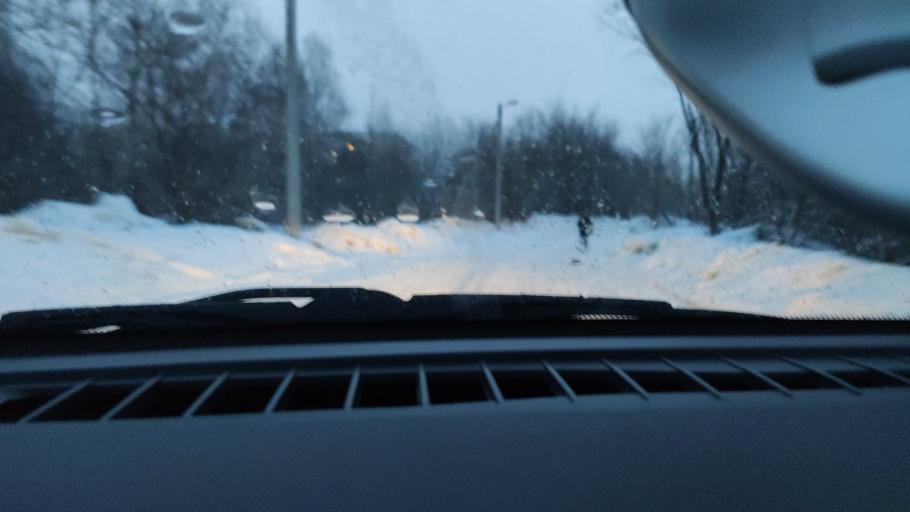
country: RU
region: Perm
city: Kondratovo
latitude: 58.0072
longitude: 56.1087
